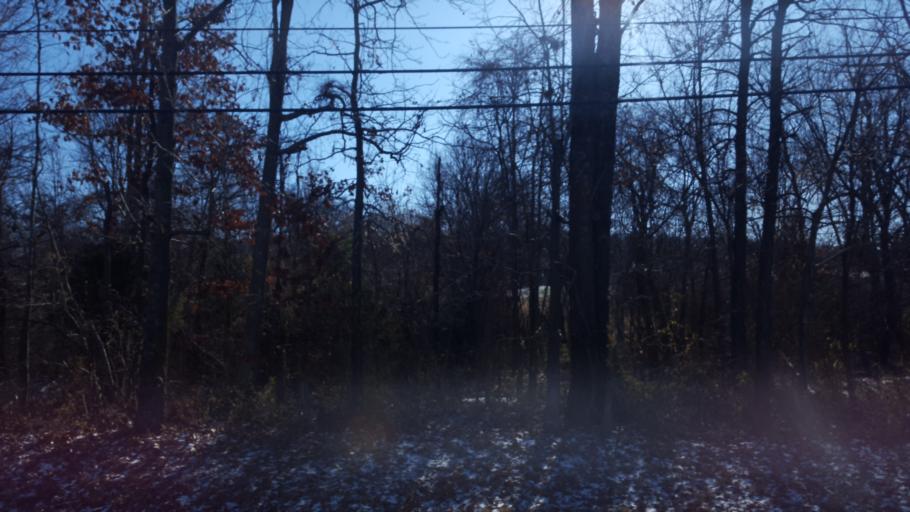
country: US
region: Kentucky
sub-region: Crittenden County
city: Marion
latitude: 37.3519
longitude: -88.0576
